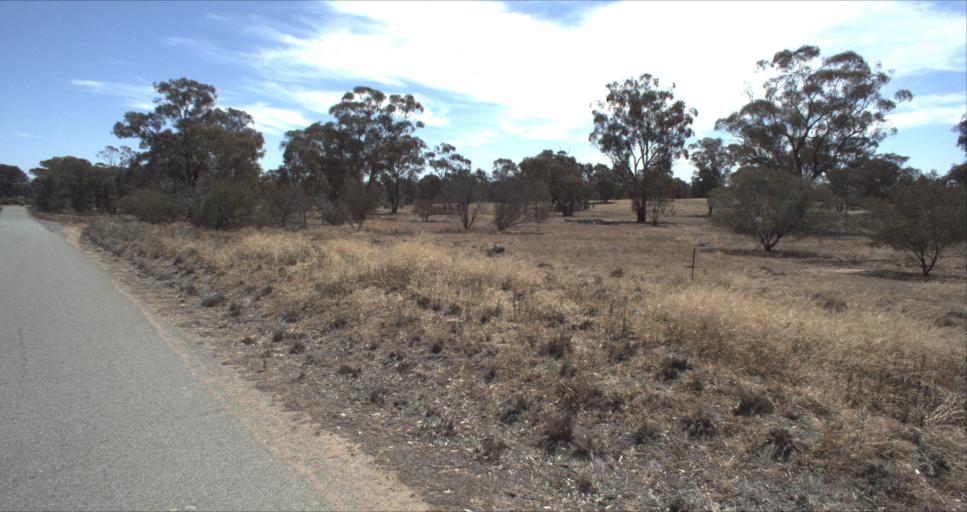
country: AU
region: New South Wales
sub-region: Leeton
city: Leeton
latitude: -34.6776
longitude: 146.4393
